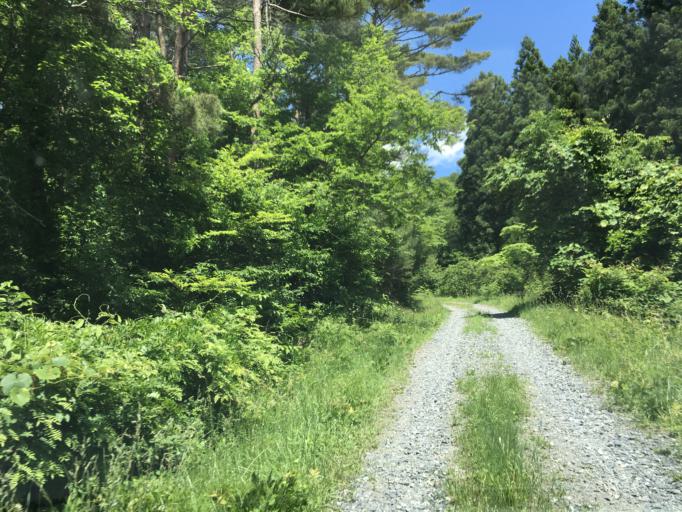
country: JP
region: Miyagi
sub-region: Oshika Gun
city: Onagawa Cho
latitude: 38.6902
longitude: 141.3546
